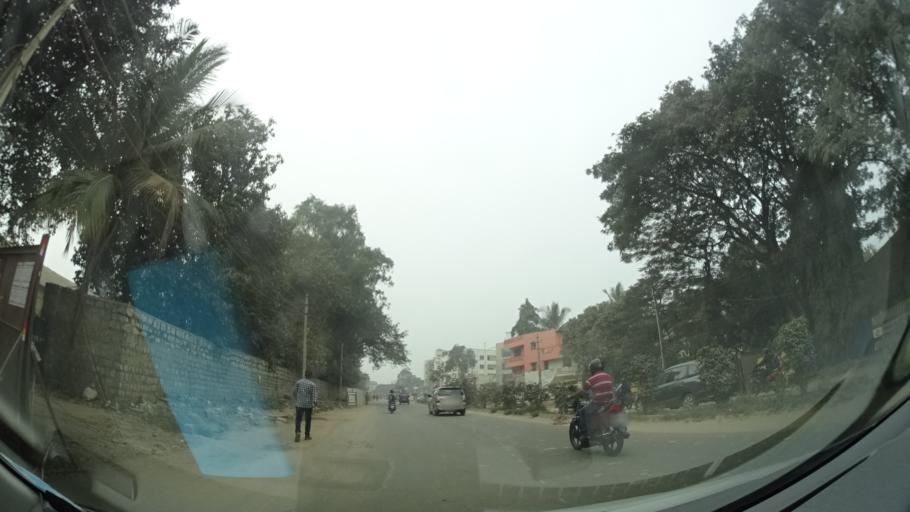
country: IN
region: Karnataka
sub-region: Bangalore Urban
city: Bangalore
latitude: 12.9874
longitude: 77.7092
